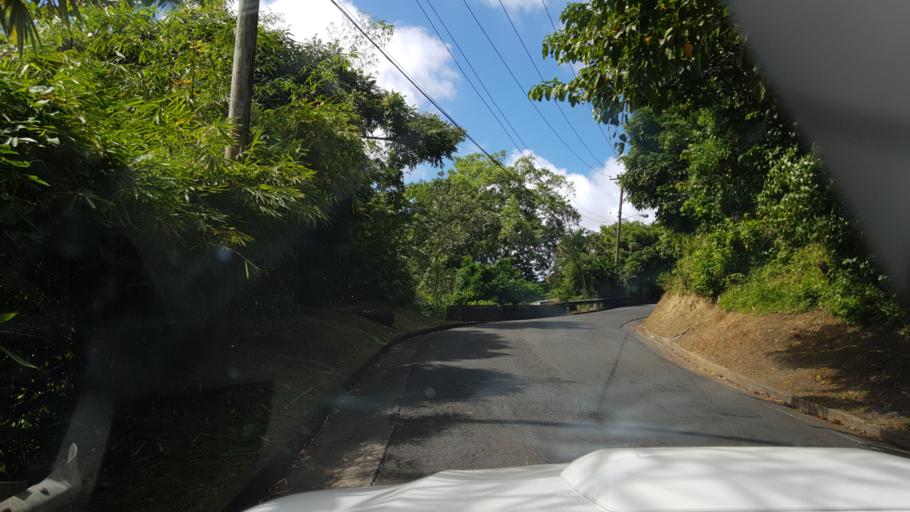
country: LC
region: Castries Quarter
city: Castries
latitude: 13.9900
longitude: -60.9734
